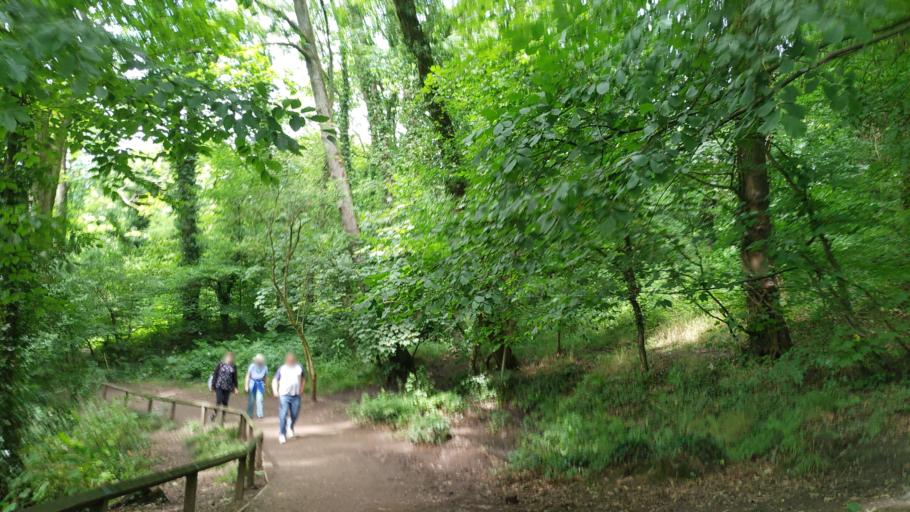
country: GB
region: England
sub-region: Lancashire
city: Coppull
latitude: 53.6305
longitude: -2.6468
